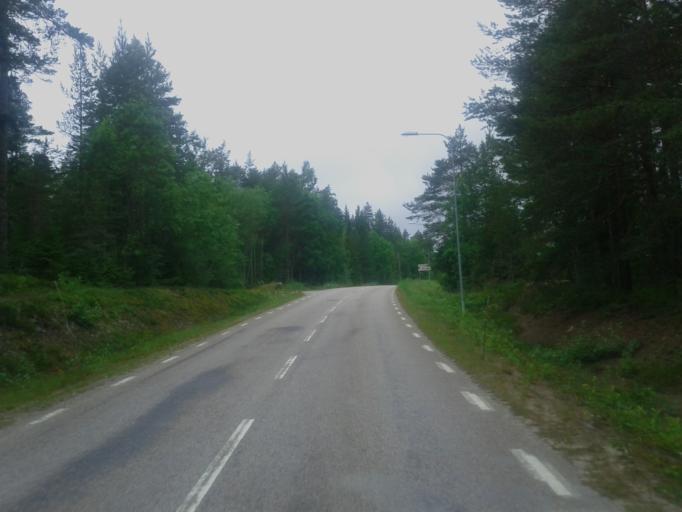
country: SE
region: Gaevleborg
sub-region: Nordanstigs Kommun
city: Bergsjoe
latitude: 61.9605
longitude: 17.3244
